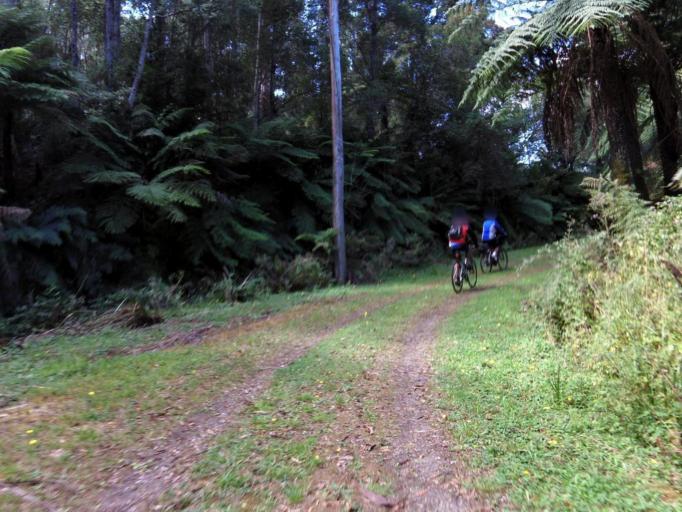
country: AU
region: Victoria
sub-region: Yarra Ranges
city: Millgrove
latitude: -37.7023
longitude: 145.7831
